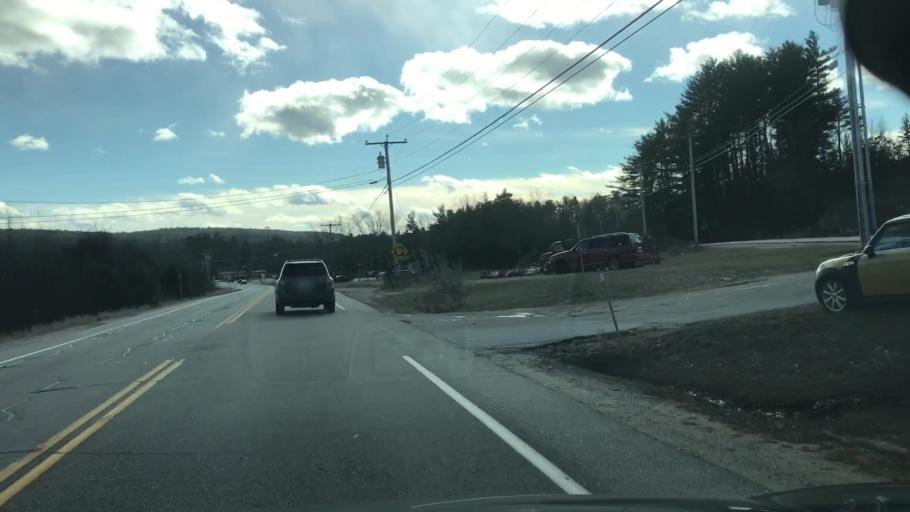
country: US
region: New Hampshire
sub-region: Merrimack County
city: Epsom
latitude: 43.2323
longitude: -71.3613
